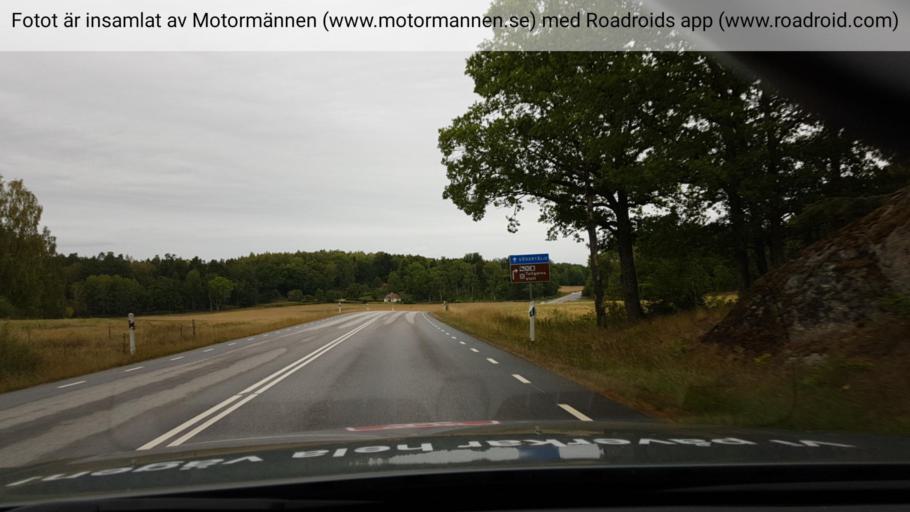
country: SE
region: Soedermanland
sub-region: Trosa Kommun
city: Vagnharad
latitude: 58.9608
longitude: 17.5605
